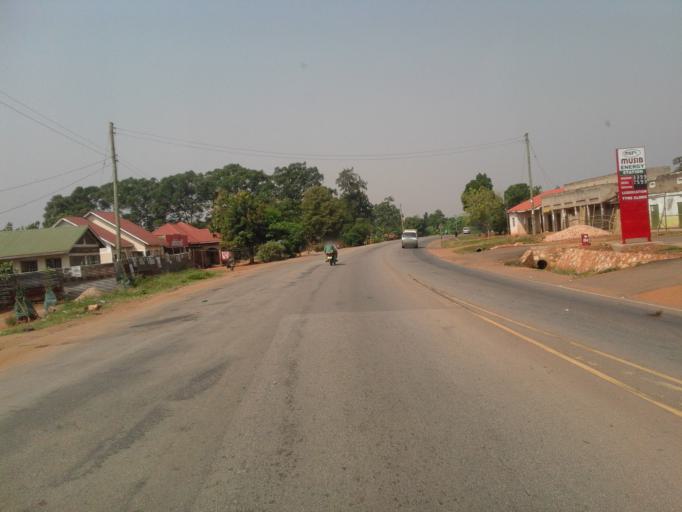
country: UG
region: Eastern Region
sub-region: Iganga District
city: Iganga
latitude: 0.6277
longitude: 33.5168
